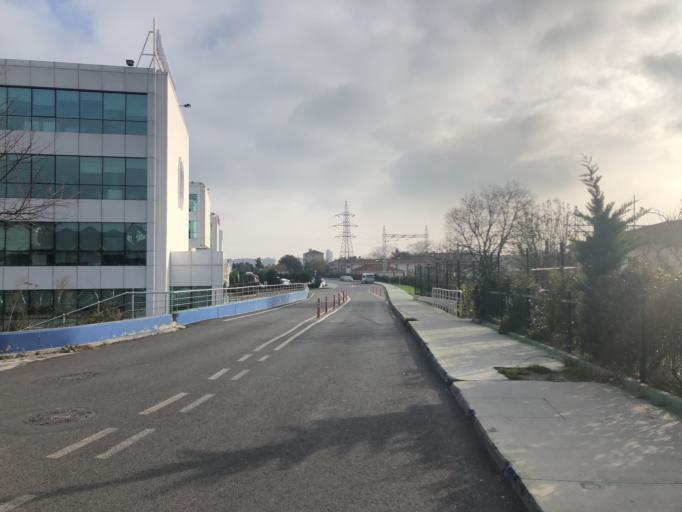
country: TR
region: Istanbul
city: merter keresteciler
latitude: 41.0187
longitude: 28.8878
